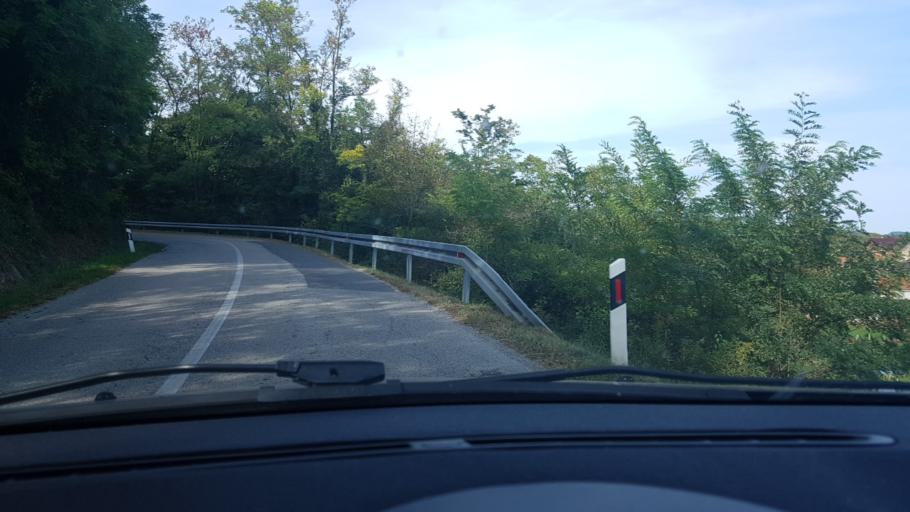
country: HR
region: Krapinsko-Zagorska
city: Zlatar
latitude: 46.1199
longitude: 16.1091
